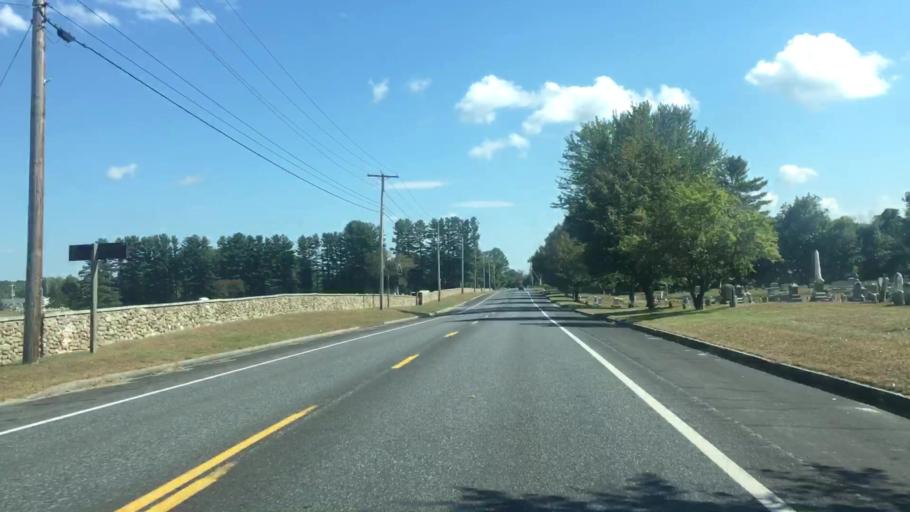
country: US
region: Maine
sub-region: Franklin County
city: Farmington
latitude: 44.6580
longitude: -70.1413
